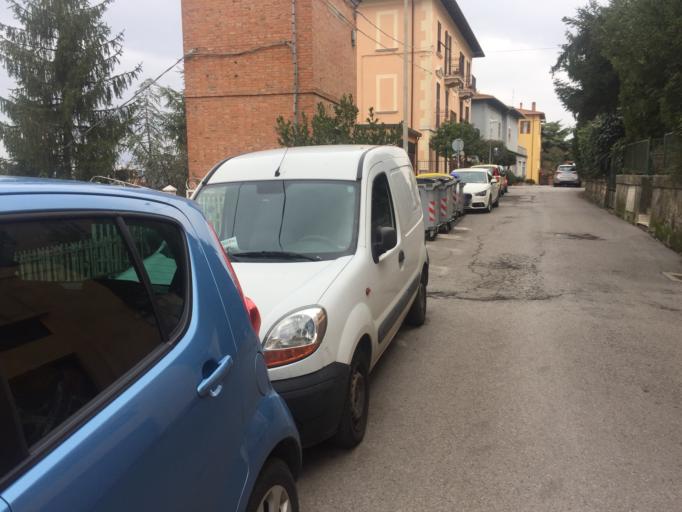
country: IT
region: Umbria
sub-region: Provincia di Perugia
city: Perugia
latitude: 43.1162
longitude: 12.3981
